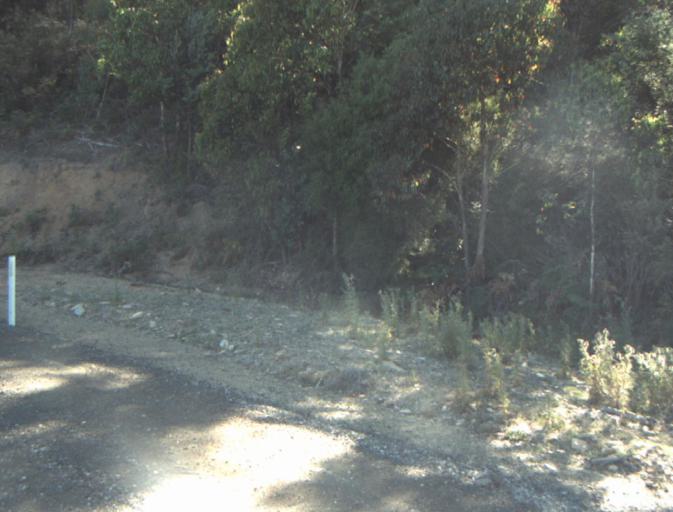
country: AU
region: Tasmania
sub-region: Launceston
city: Newstead
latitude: -41.2949
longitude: 147.3409
